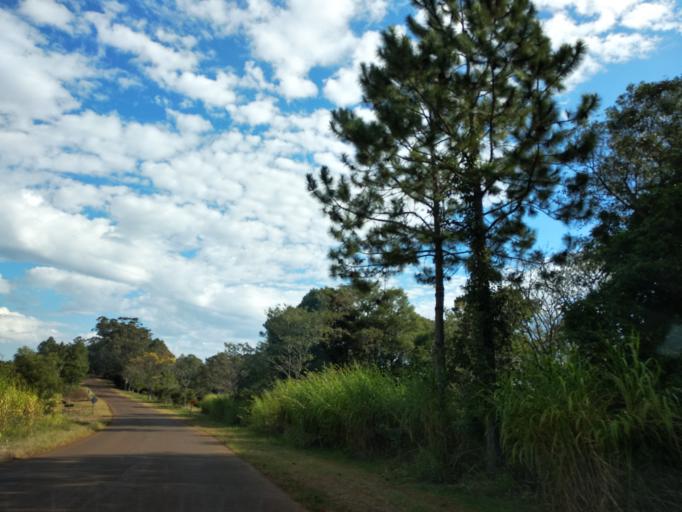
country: AR
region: Misiones
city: Aristobulo del Valle
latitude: -27.0713
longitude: -54.8299
